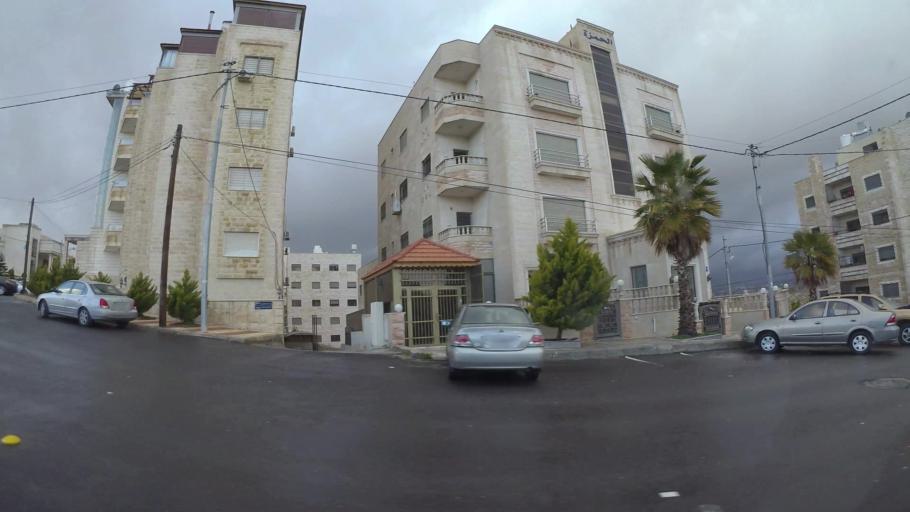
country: JO
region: Amman
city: Amman
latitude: 32.0037
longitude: 35.9271
